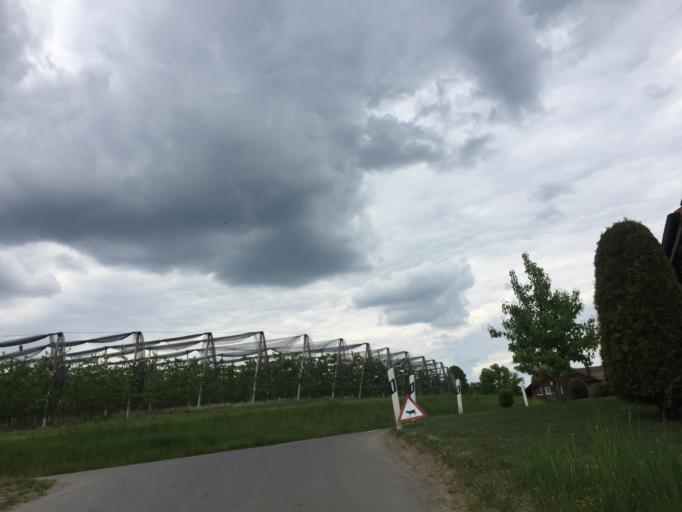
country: CH
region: Bern
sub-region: Thun District
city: Seftigen
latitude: 46.8031
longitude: 7.5486
